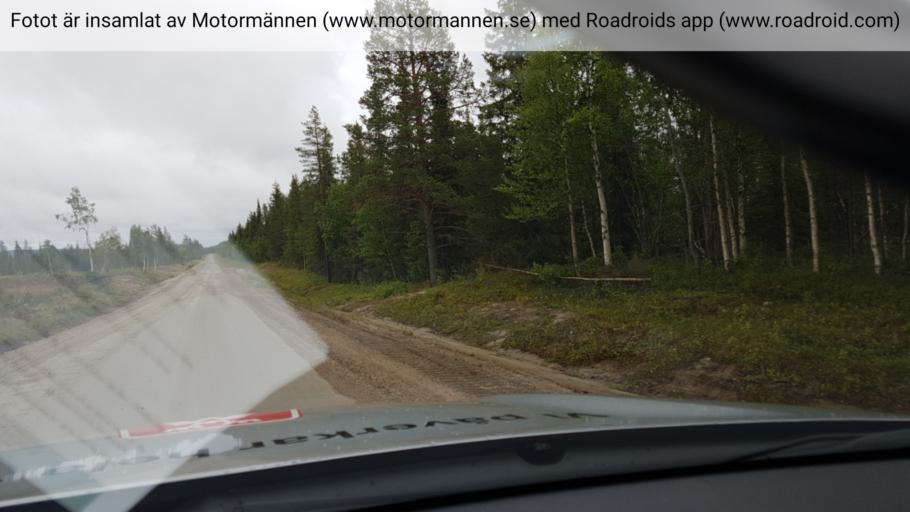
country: SE
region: Norrbotten
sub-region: Gallivare Kommun
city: Gaellivare
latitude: 66.7413
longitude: 20.8556
